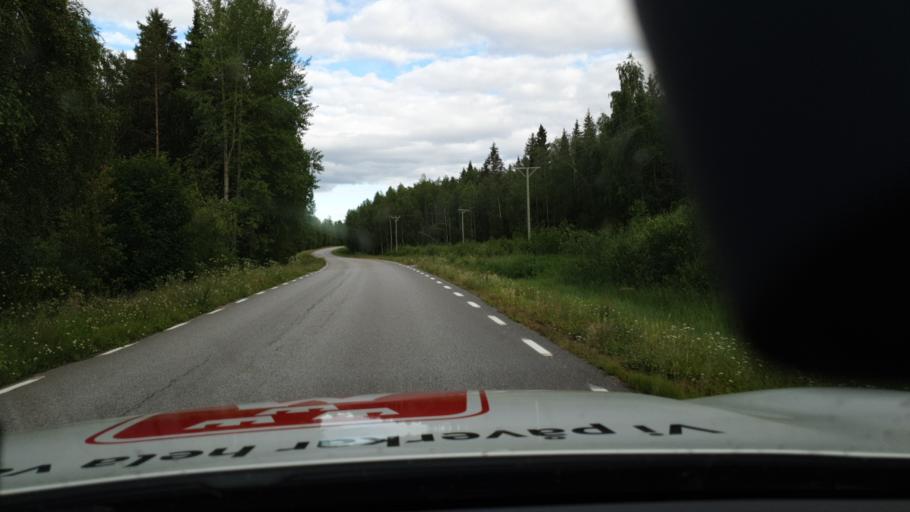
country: SE
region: Norrbotten
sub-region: Kalix Kommun
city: Toere
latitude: 65.8912
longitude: 22.6429
